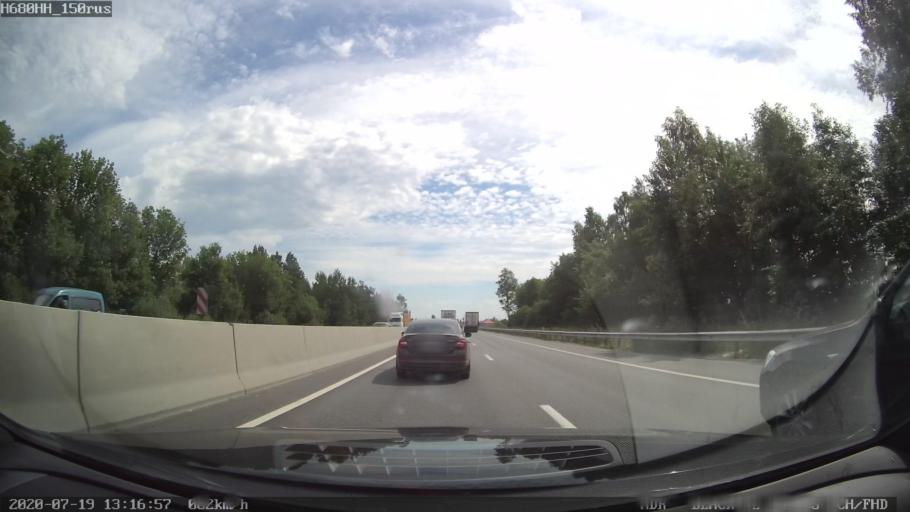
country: RU
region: St.-Petersburg
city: Kolpino
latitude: 59.7131
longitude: 30.5623
